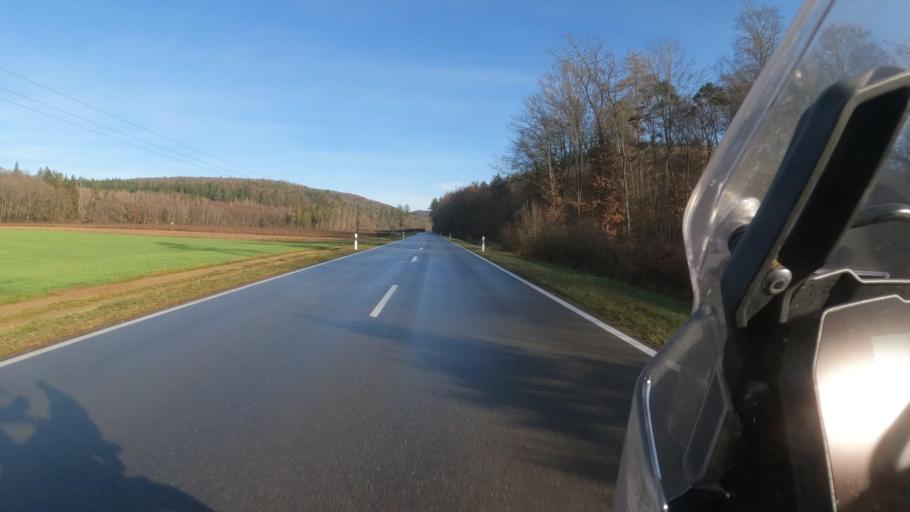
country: DE
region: Baden-Wuerttemberg
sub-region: Freiburg Region
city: Muhlhausen-Ehingen
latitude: 47.8426
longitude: 8.8182
